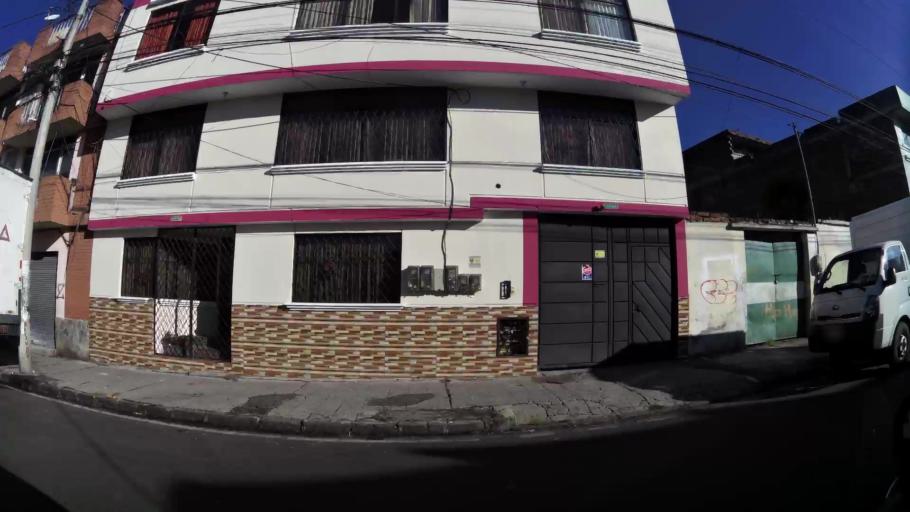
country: EC
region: Pichincha
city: Quito
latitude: -0.2435
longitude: -78.5145
